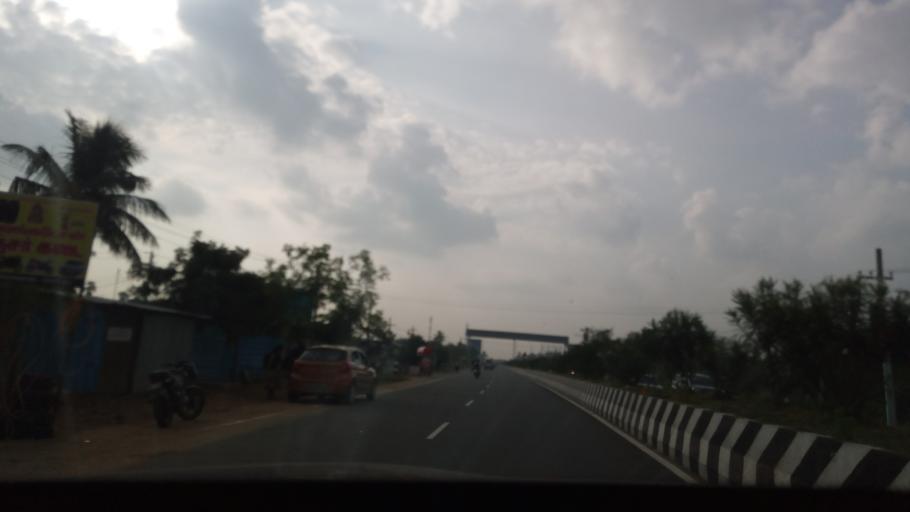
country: IN
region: Tamil Nadu
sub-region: Kancheepuram
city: Injambakkam
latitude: 12.7840
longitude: 80.2455
